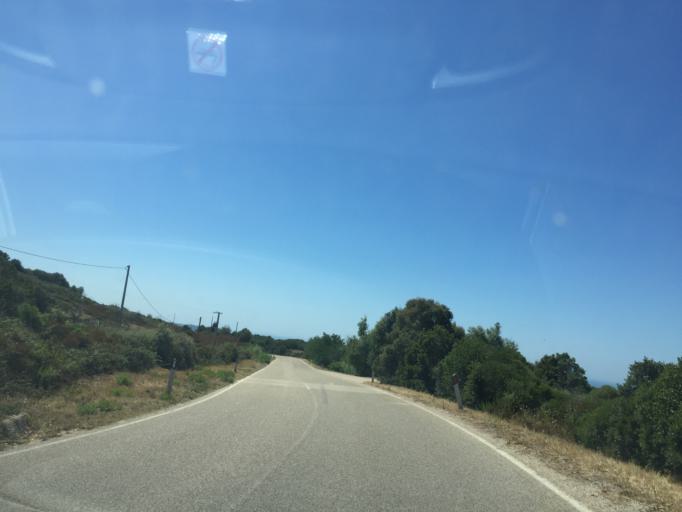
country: IT
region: Sardinia
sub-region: Provincia di Olbia-Tempio
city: Aglientu
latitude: 41.0892
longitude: 9.1175
